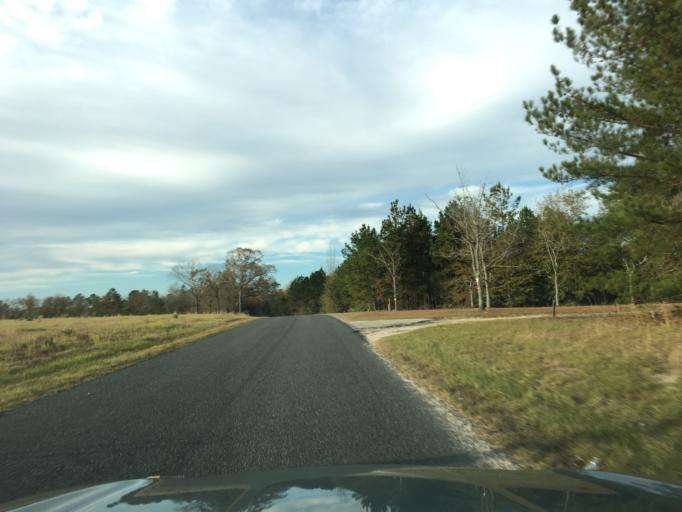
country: US
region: South Carolina
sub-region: Lexington County
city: Leesville
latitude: 33.6792
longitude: -81.3755
